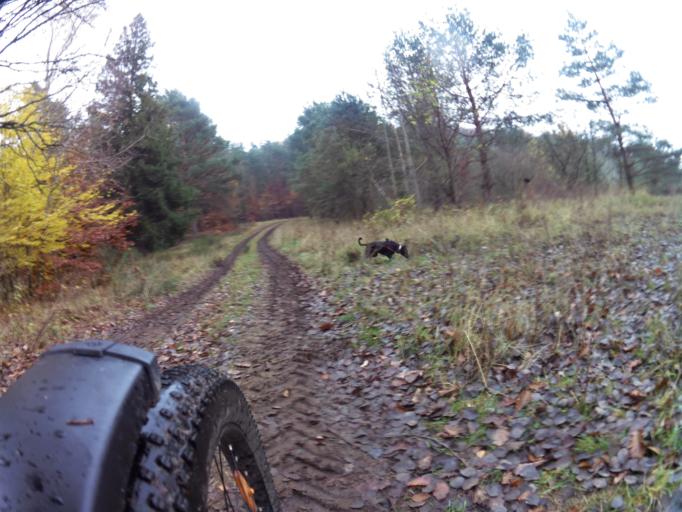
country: PL
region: Pomeranian Voivodeship
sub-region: Powiat pucki
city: Krokowa
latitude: 54.7442
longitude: 18.1007
